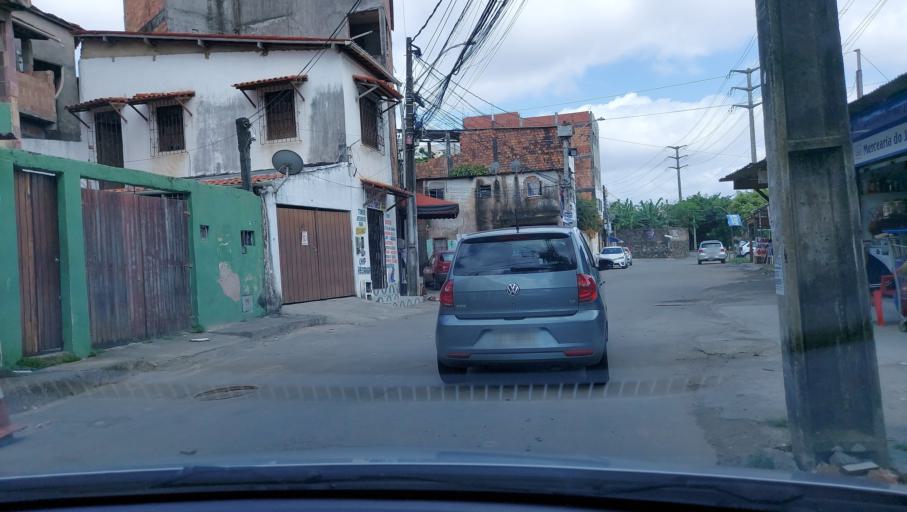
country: BR
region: Bahia
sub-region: Salvador
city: Salvador
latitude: -12.9678
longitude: -38.4289
